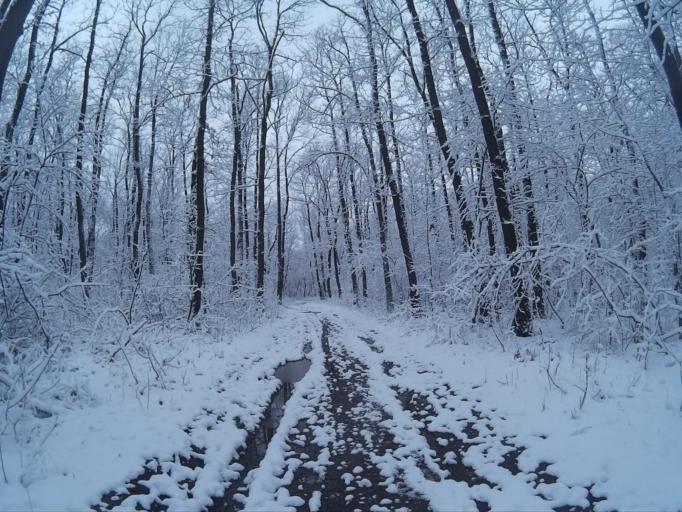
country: HU
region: Fejer
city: Szarliget
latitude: 47.5132
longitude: 18.5177
